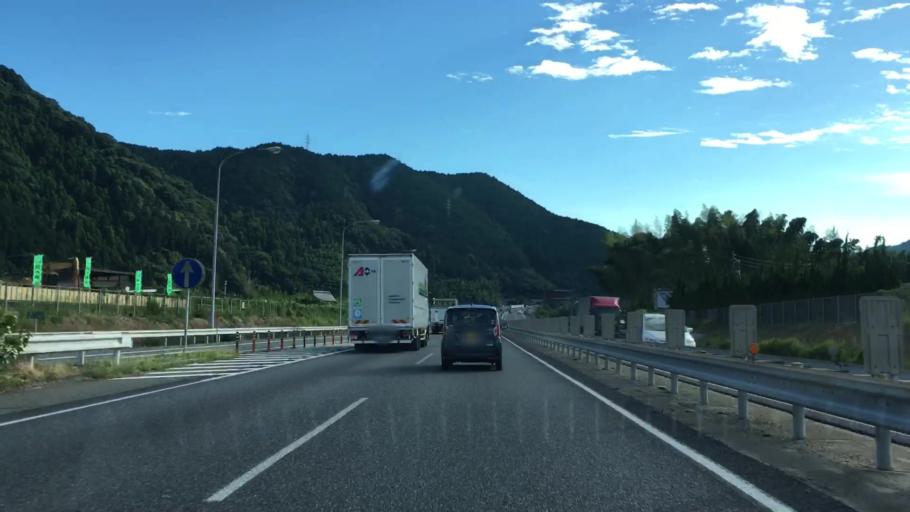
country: JP
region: Yamaguchi
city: Iwakuni
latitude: 34.1738
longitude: 132.1647
